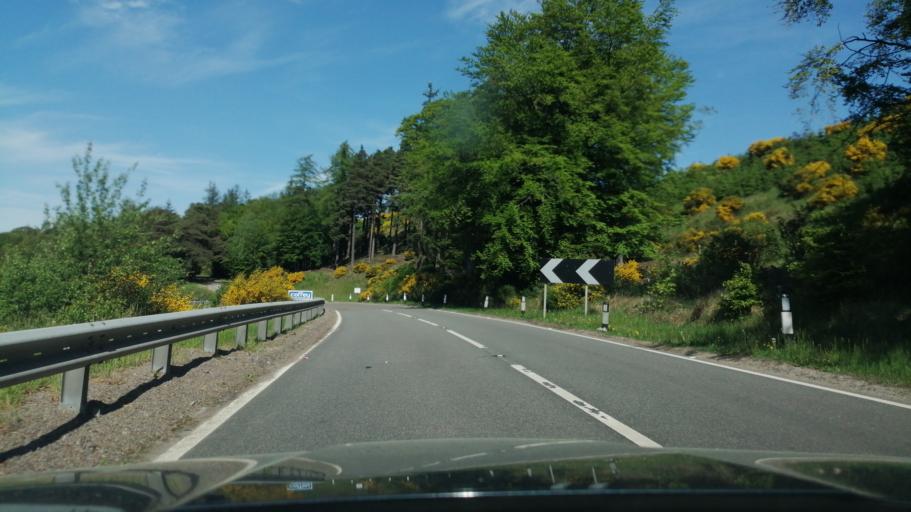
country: GB
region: Scotland
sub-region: Moray
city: Rothes
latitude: 57.4885
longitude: -3.1683
